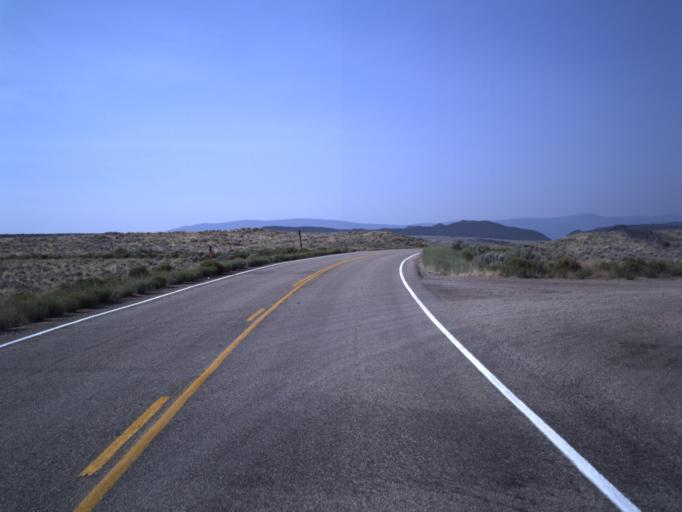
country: US
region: Utah
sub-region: Daggett County
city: Manila
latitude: 40.9948
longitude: -109.4335
